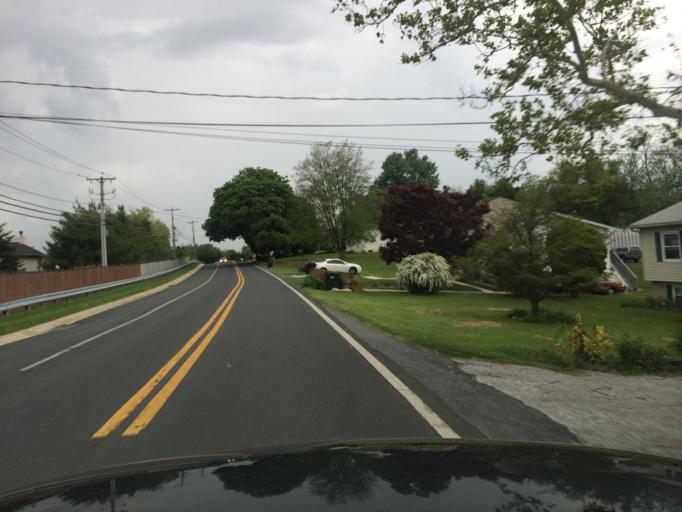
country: US
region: Maryland
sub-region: Carroll County
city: Eldersburg
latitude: 39.4172
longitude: -76.9586
